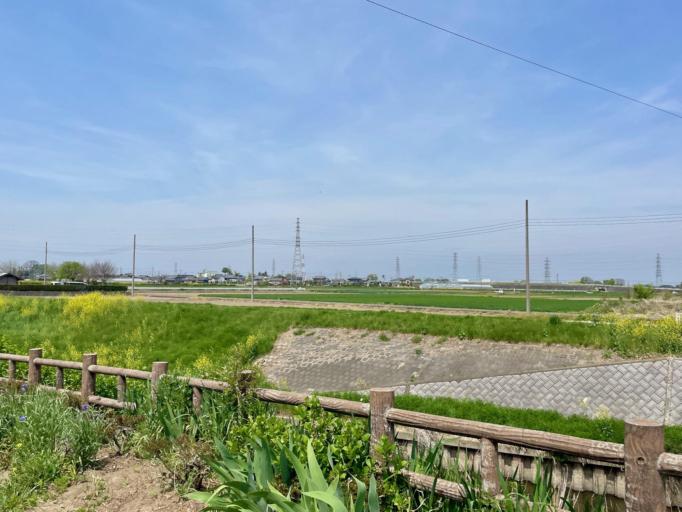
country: JP
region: Saitama
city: Fukayacho
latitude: 36.2052
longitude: 139.2986
